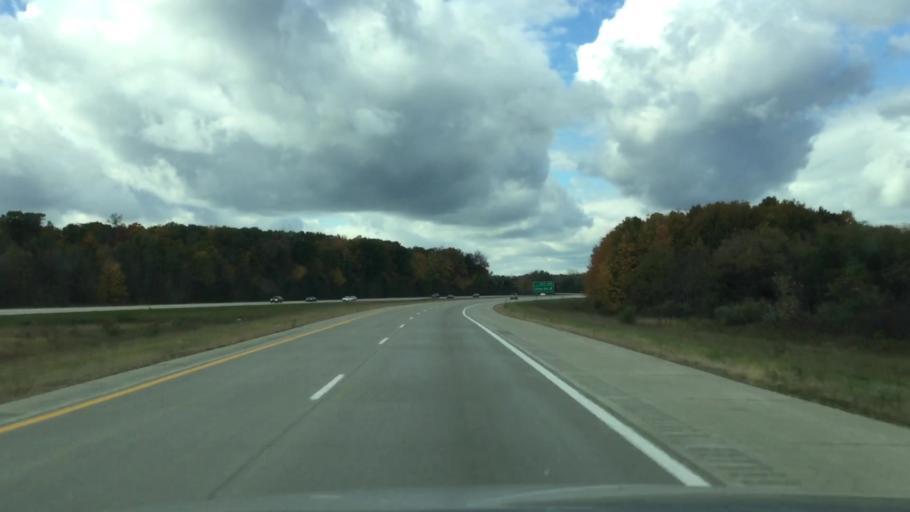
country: US
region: Michigan
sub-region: Genesee County
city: Davison
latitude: 43.0167
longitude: -83.4277
